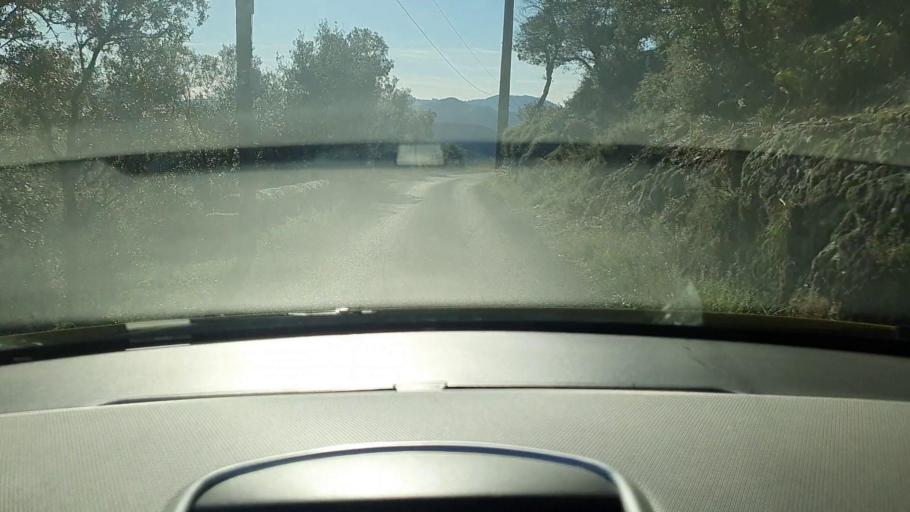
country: FR
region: Languedoc-Roussillon
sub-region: Departement du Gard
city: Sumene
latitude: 44.0357
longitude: 3.7110
